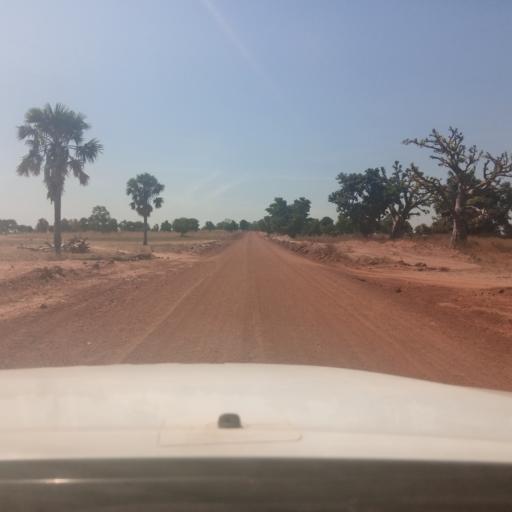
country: NG
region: Adamawa
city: Yola
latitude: 9.1932
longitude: 12.8712
